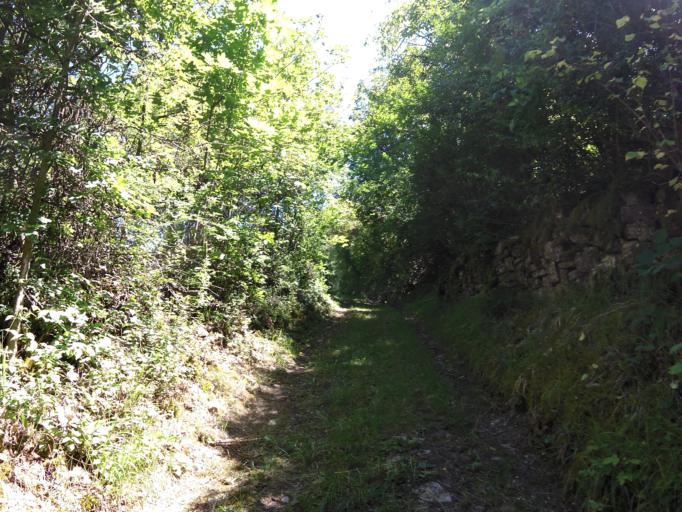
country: DE
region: Bavaria
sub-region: Regierungsbezirk Unterfranken
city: Randersacker
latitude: 49.7590
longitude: 9.9868
